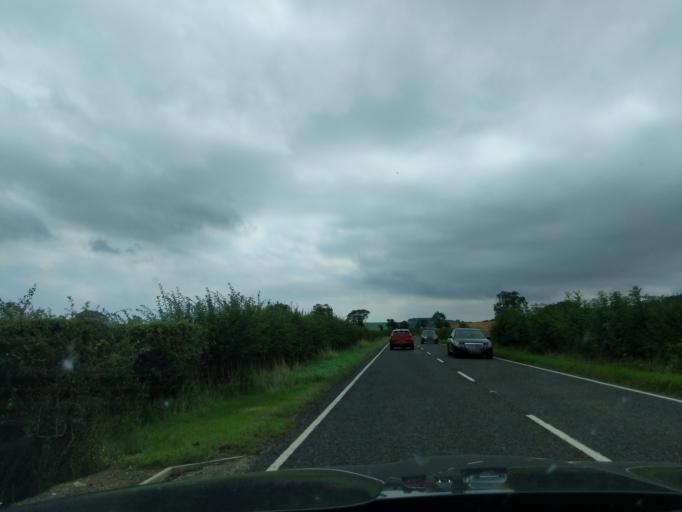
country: GB
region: England
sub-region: Northumberland
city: Whittingham
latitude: 55.3986
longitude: -1.8595
